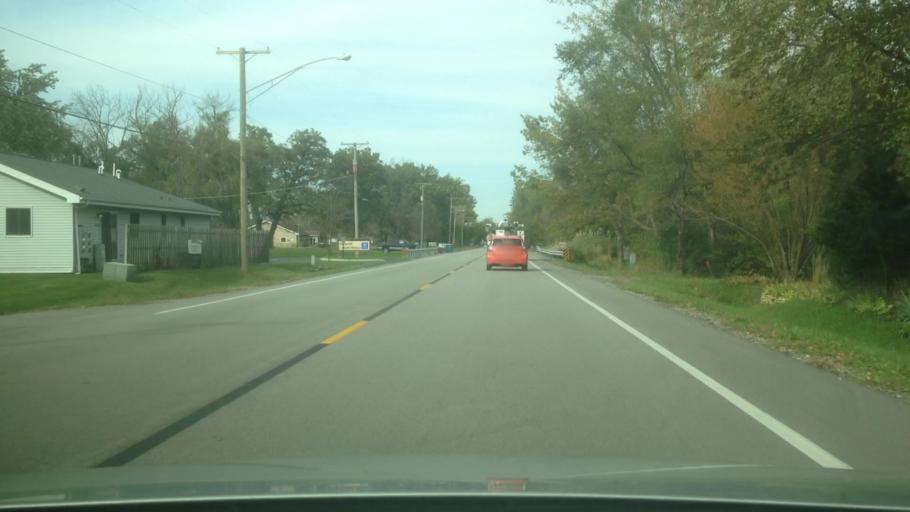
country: US
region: Illinois
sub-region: Will County
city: Wilmington
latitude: 41.2999
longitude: -88.1587
